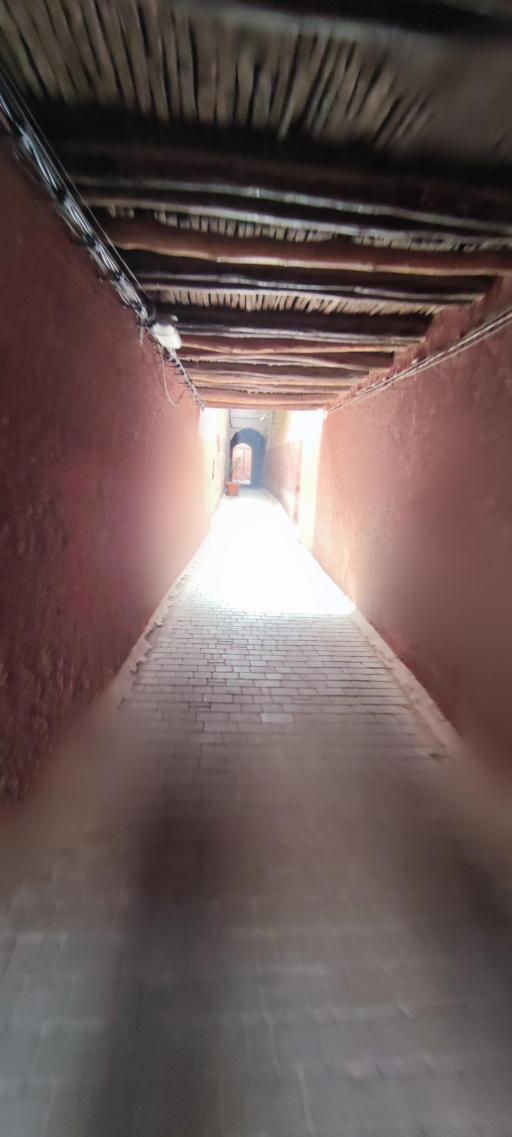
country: MA
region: Marrakech-Tensift-Al Haouz
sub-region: Marrakech
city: Marrakesh
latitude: 31.6325
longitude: -7.9912
